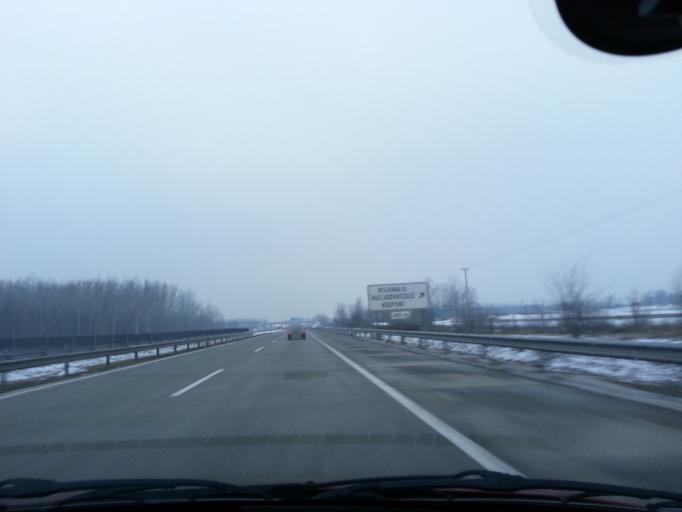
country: HU
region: Pest
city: Gyal
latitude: 47.3704
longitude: 19.2433
